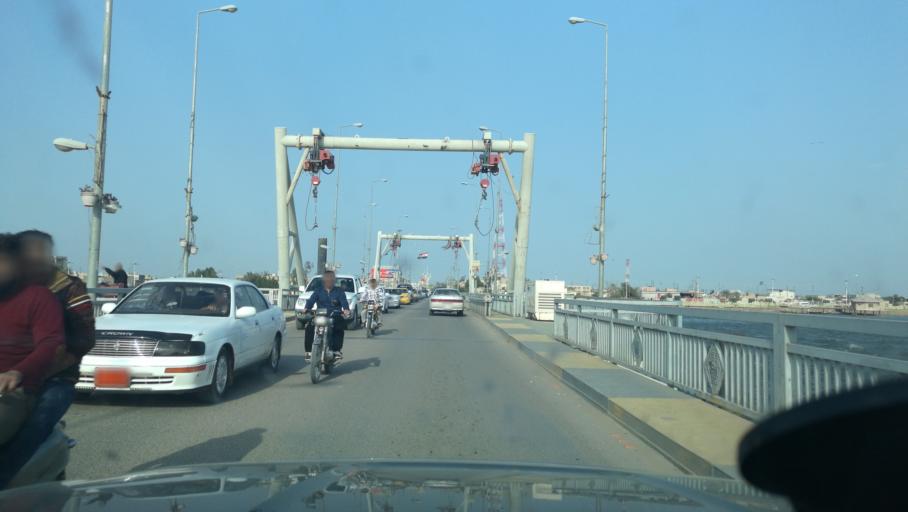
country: IQ
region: Basra Governorate
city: Al Basrah al Qadimah
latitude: 30.5224
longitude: 47.8433
